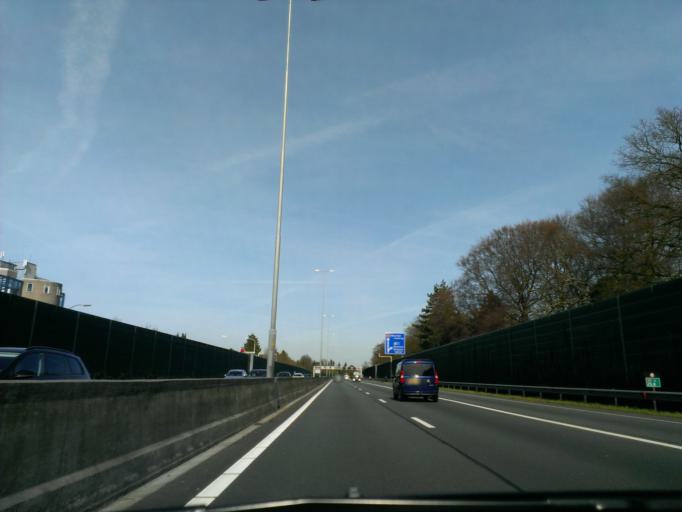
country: NL
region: North Holland
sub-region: Gemeente Bussum
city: Bussum
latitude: 52.2732
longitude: 5.1927
